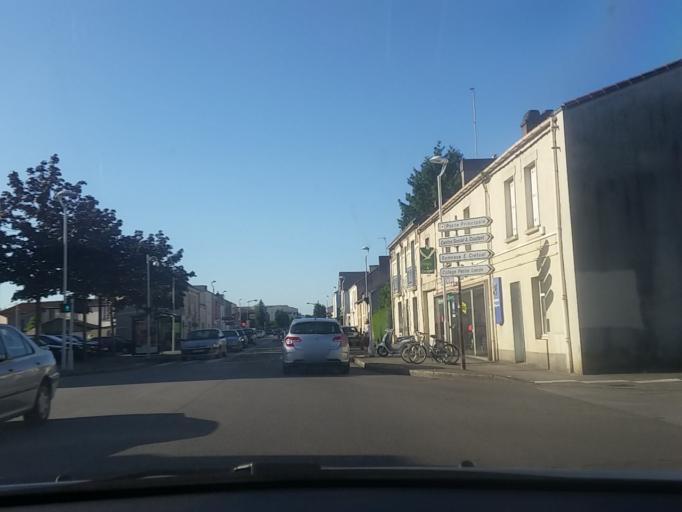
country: FR
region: Pays de la Loire
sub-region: Departement de la Loire-Atlantique
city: Reze
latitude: 47.1784
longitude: -1.5445
